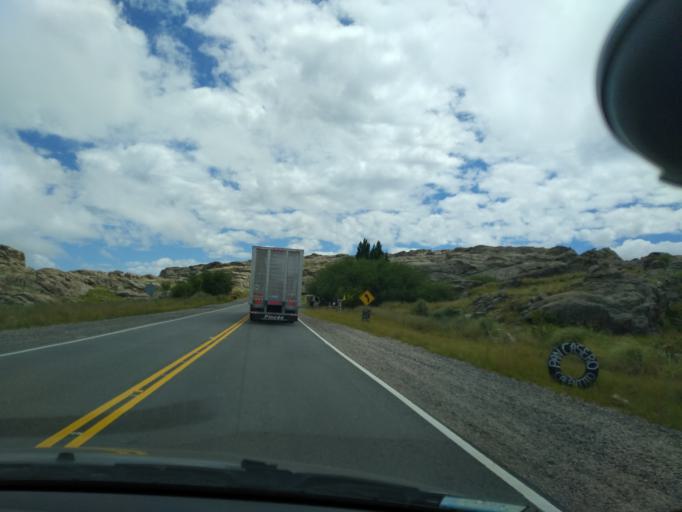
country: AR
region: Cordoba
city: Mina Clavero
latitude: -31.6362
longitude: -64.9078
